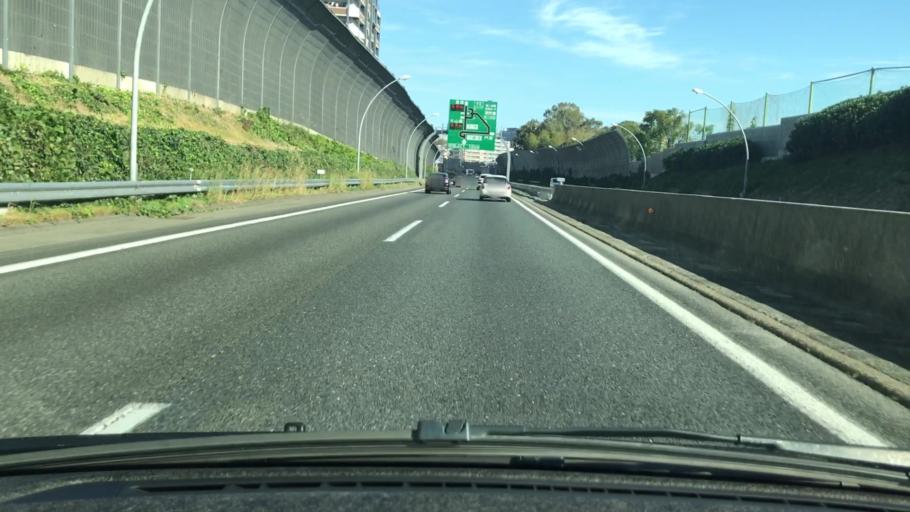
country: JP
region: Osaka
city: Suita
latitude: 34.7887
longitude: 135.5326
